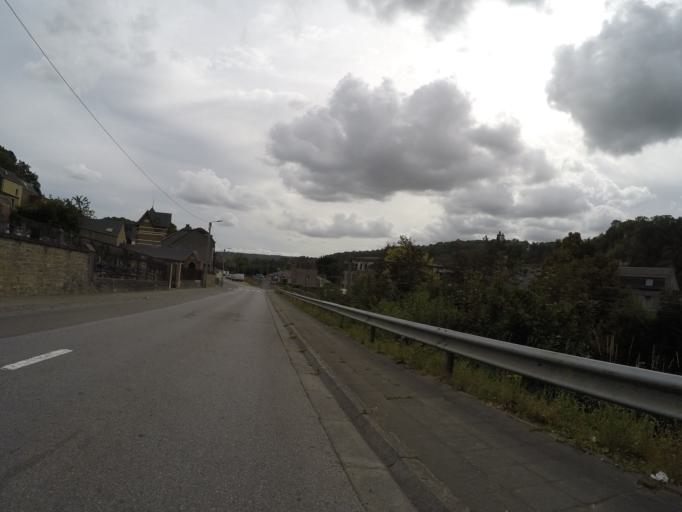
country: BE
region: Wallonia
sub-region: Province de Namur
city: Yvoir
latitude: 50.3301
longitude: 4.8753
